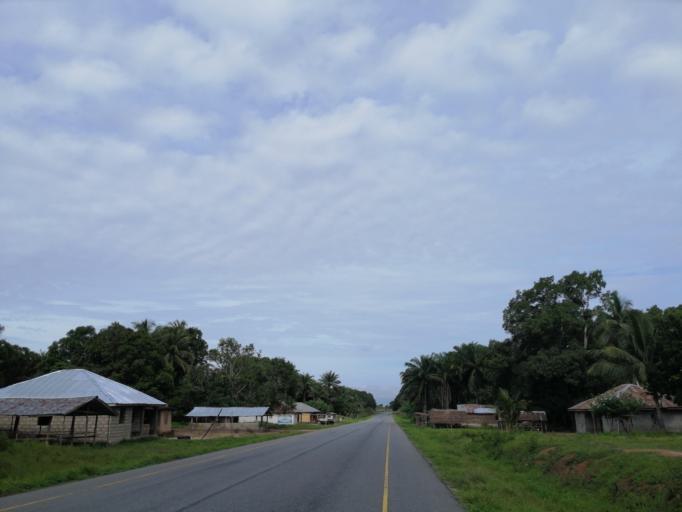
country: SL
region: Northern Province
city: Port Loko
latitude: 8.7721
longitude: -12.8681
